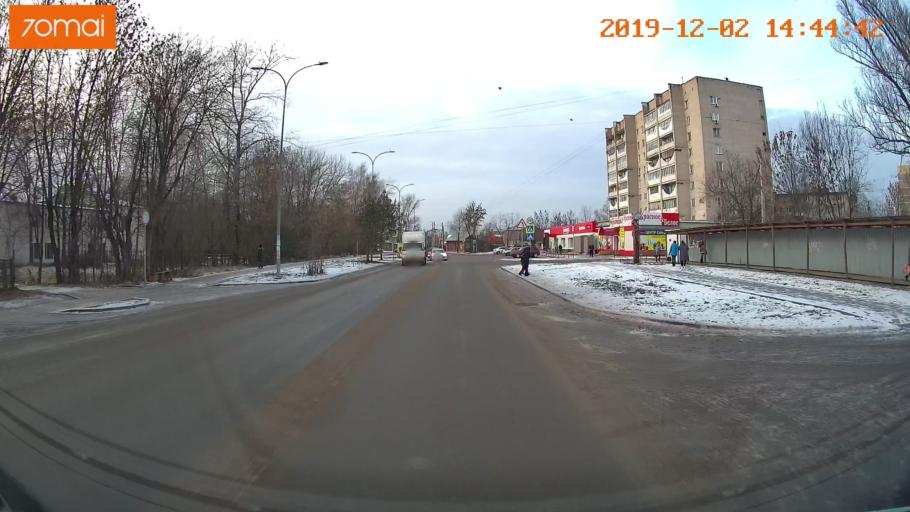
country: RU
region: Ivanovo
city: Bogorodskoye
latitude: 56.9897
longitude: 41.0356
